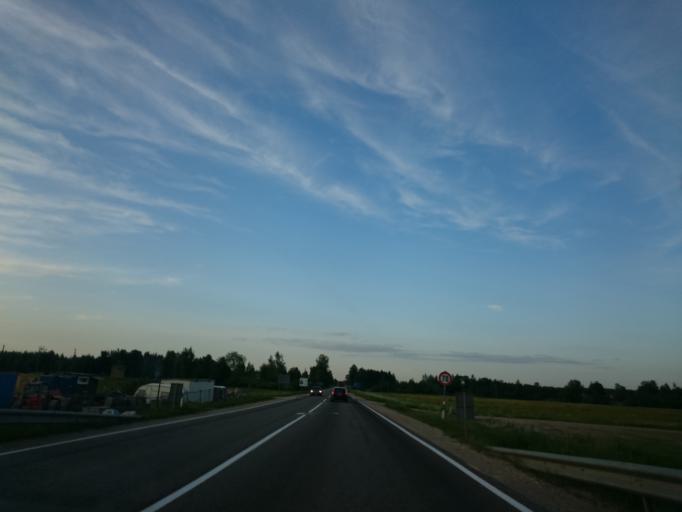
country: LV
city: Tireli
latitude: 56.8372
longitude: 23.5802
